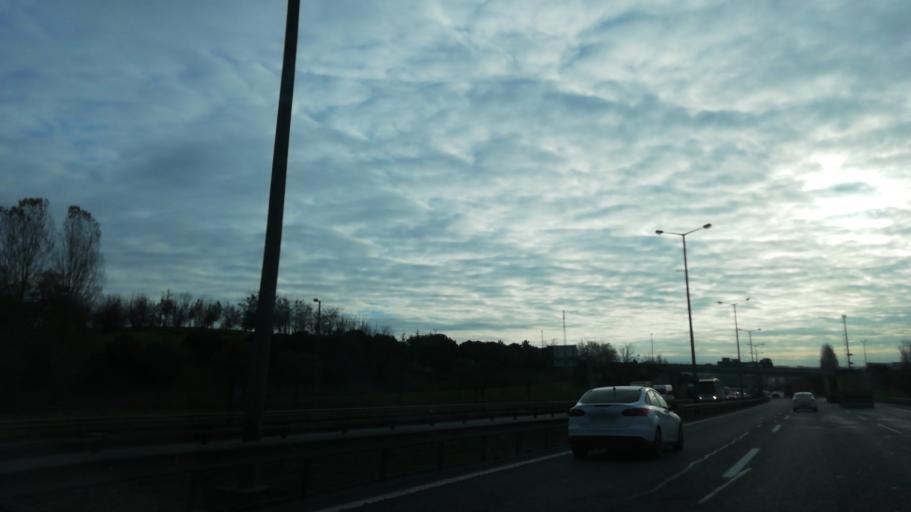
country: TR
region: Istanbul
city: Sultanbeyli
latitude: 40.9375
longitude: 29.3298
